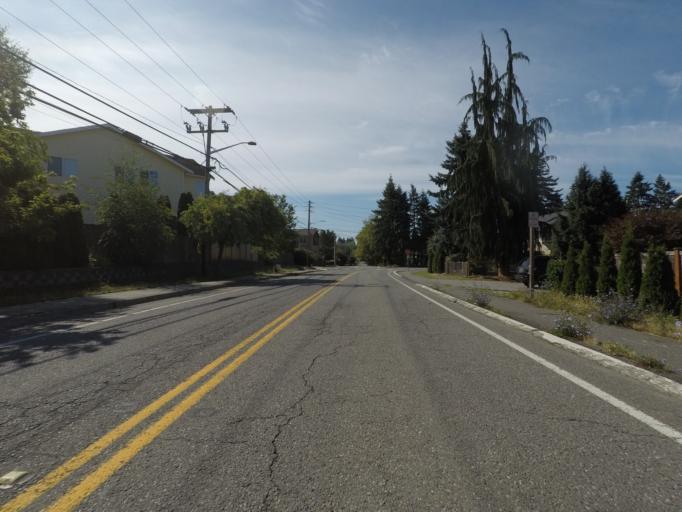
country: US
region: Washington
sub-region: King County
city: Inglewood-Finn Hill
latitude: 47.7123
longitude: -122.2296
